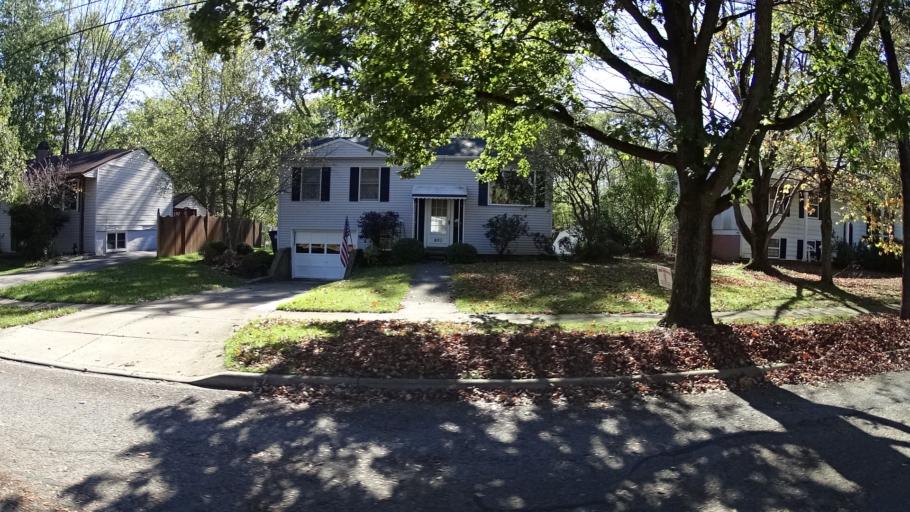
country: US
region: Ohio
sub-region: Lorain County
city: Oberlin
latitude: 41.2921
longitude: -82.1919
